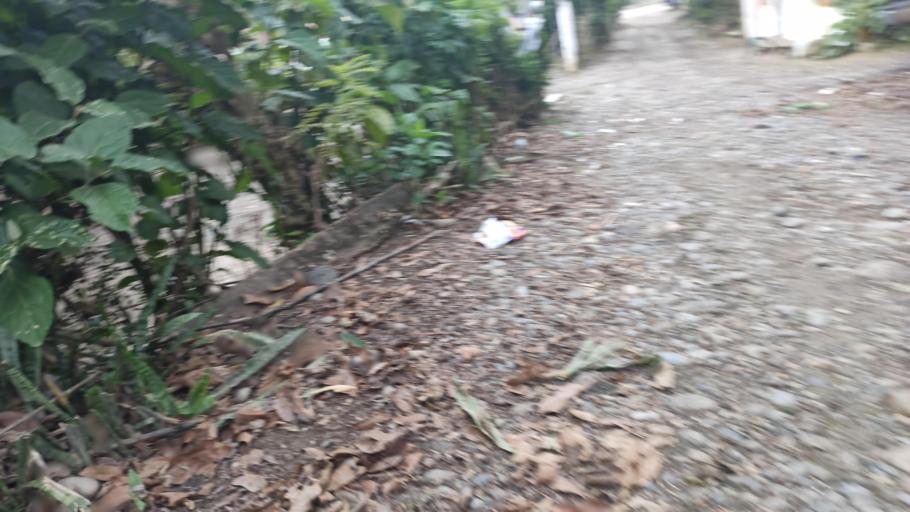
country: MX
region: Veracruz
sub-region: Coatzintla
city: Manuel Maria Contreras
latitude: 20.3613
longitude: -97.5136
